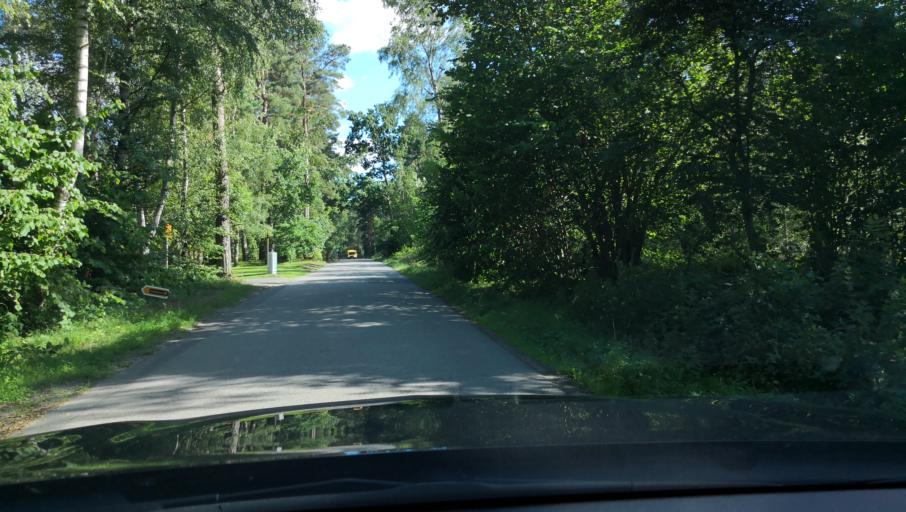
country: SE
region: Skane
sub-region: Simrishamns Kommun
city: Kivik
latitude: 55.7792
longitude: 14.1942
